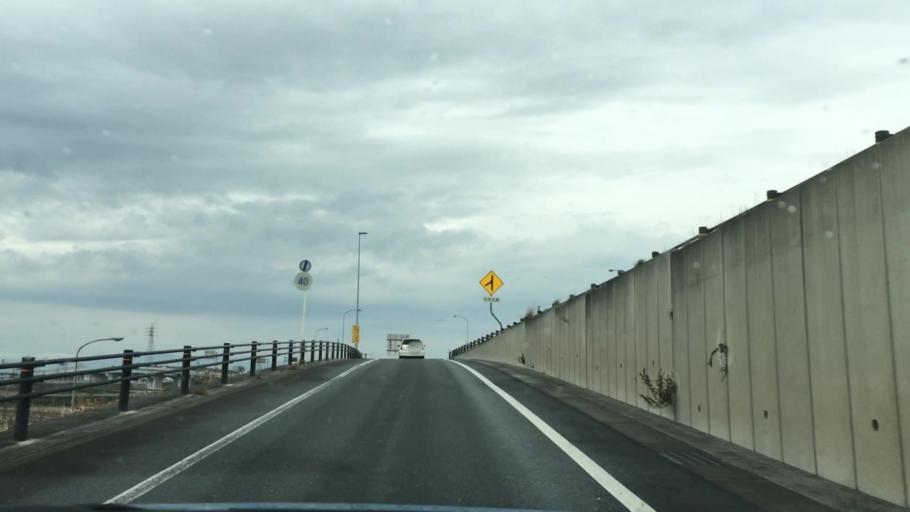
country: JP
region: Aichi
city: Toyohashi
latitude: 34.7285
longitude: 137.3541
